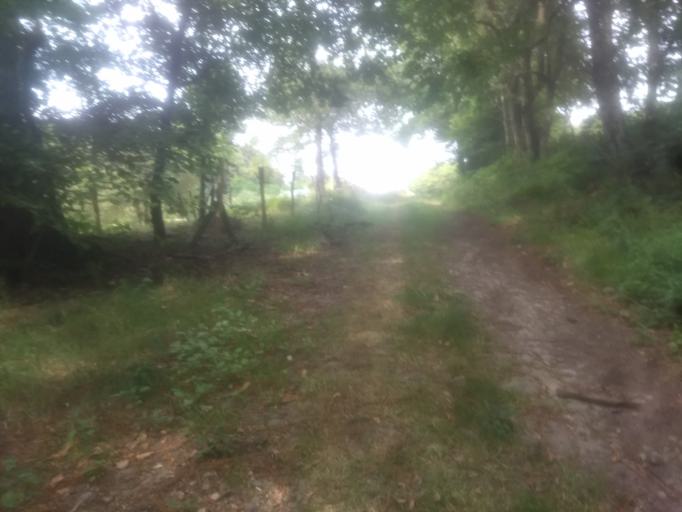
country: FR
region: Limousin
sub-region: Departement de la Haute-Vienne
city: Ambazac
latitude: 46.0351
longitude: 1.5197
